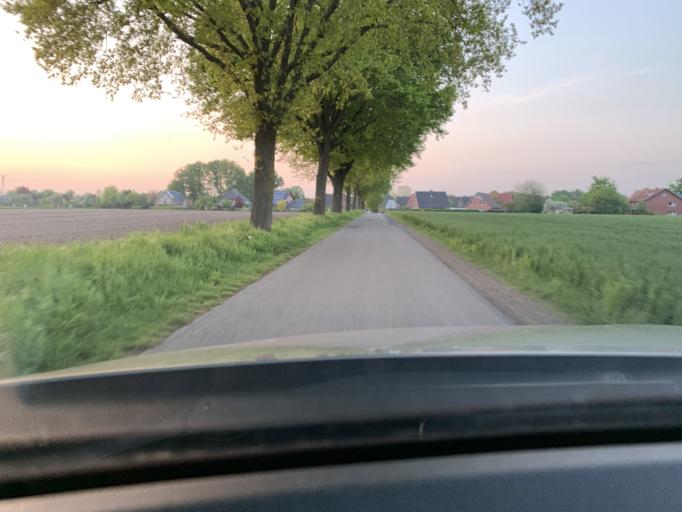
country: DE
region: North Rhine-Westphalia
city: Rietberg
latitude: 51.7973
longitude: 8.3833
